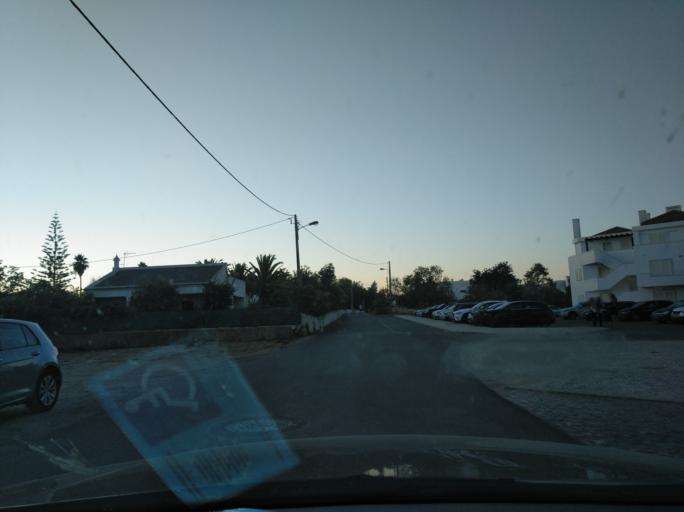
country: PT
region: Faro
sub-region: Tavira
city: Tavira
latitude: 37.1376
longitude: -7.5966
